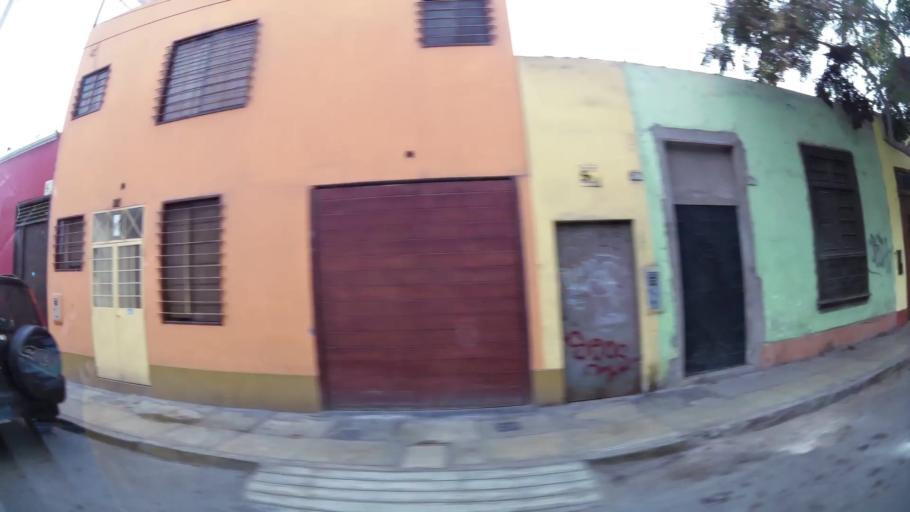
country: PE
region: Lima
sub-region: Lima
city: Surco
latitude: -12.1429
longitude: -77.0216
